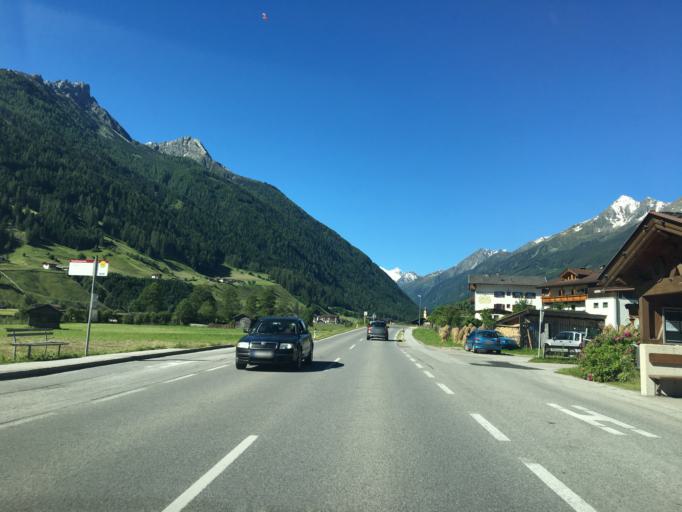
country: AT
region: Tyrol
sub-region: Politischer Bezirk Innsbruck Land
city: Neustift im Stubaital
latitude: 47.1206
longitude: 11.3213
